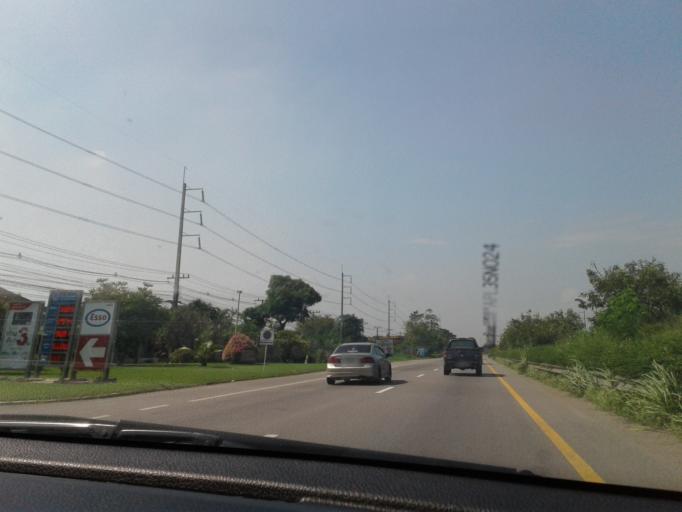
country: TH
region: Ratchaburi
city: Photharam
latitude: 13.6563
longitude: 99.8649
